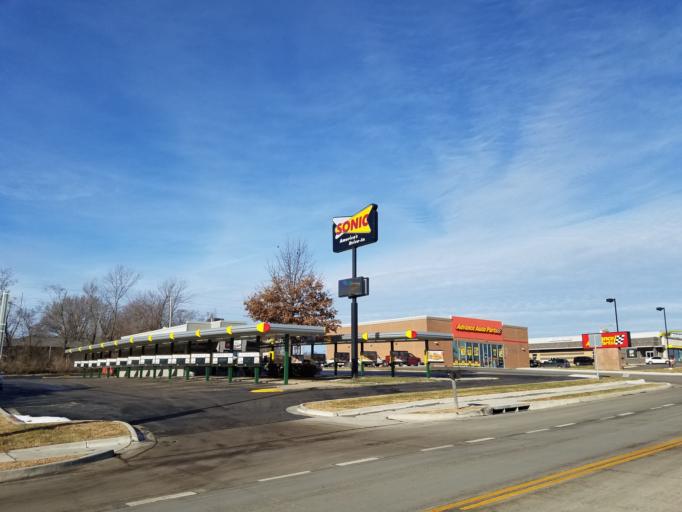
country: US
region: Missouri
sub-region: Jackson County
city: Grain Valley
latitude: 39.0170
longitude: -94.1983
